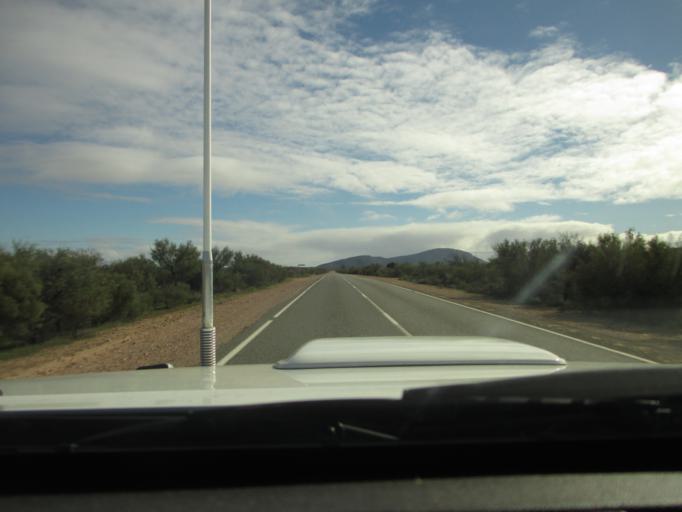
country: AU
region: South Australia
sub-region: Flinders Ranges
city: Quorn
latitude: -31.8427
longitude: 138.3922
